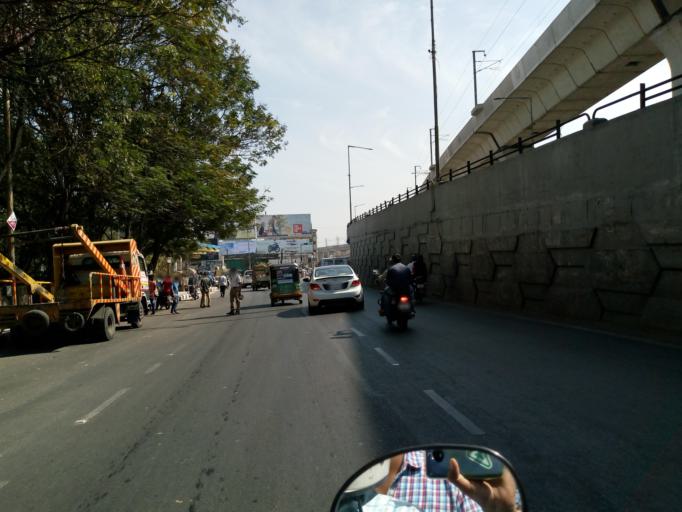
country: IN
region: Telangana
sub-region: Hyderabad
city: Malkajgiri
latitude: 17.4276
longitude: 78.5301
